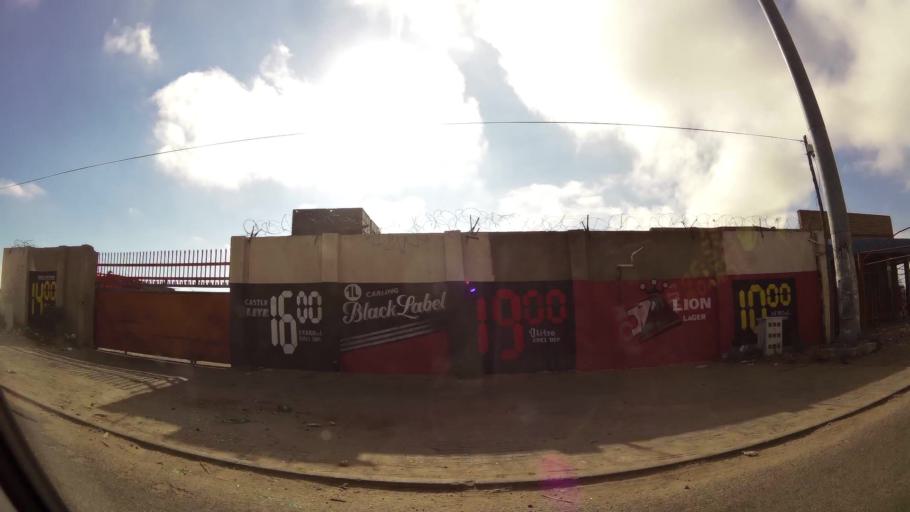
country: ZA
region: Limpopo
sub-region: Capricorn District Municipality
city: Polokwane
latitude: -23.8512
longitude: 29.3824
